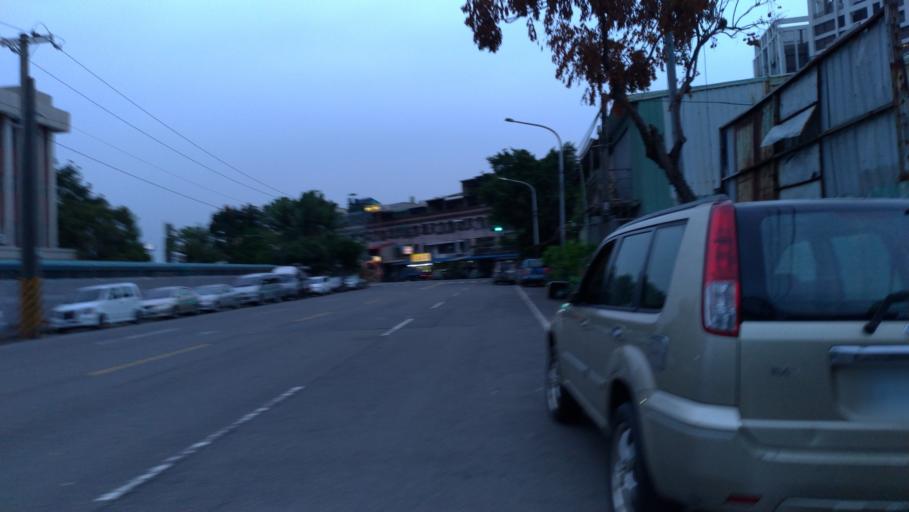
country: TW
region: Taiwan
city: Fengshan
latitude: 22.6547
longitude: 120.3626
